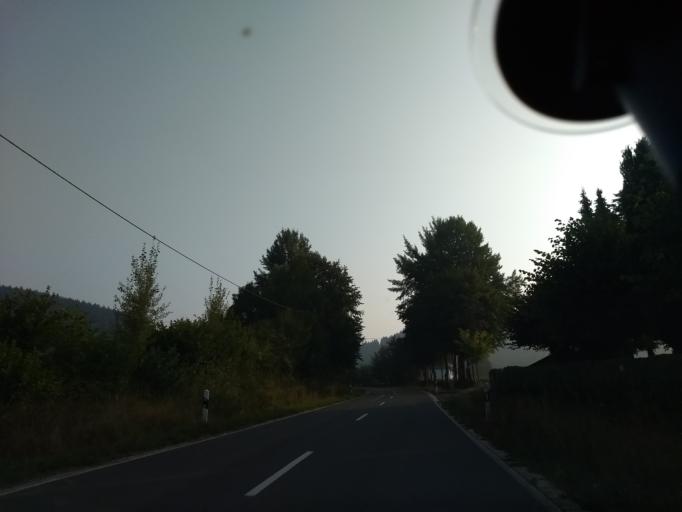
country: DE
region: North Rhine-Westphalia
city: Eslohe
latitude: 51.2160
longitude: 8.0849
